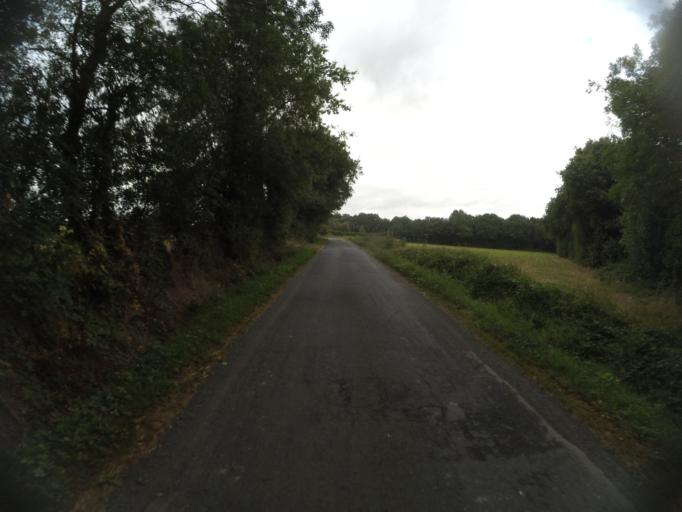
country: FR
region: Pays de la Loire
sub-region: Departement de la Vendee
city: Saint-Hilaire-de-Loulay
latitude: 47.0241
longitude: -1.3175
